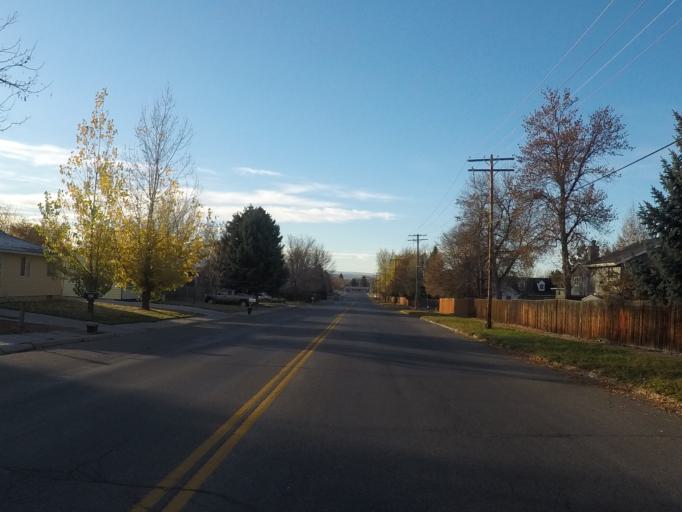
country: US
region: Montana
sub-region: Yellowstone County
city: Billings
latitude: 45.7886
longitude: -108.5903
